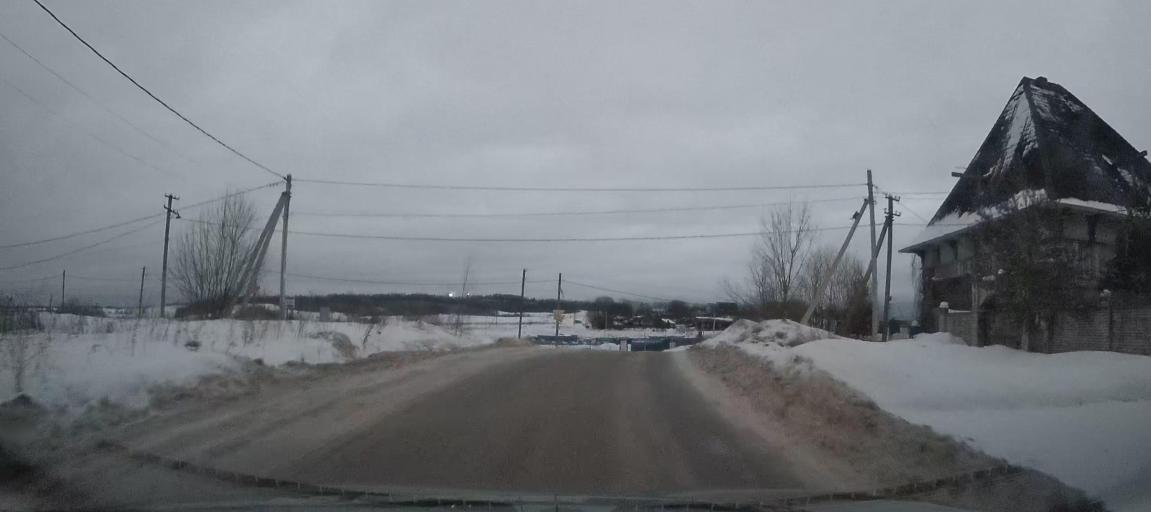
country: RU
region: Leningrad
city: Taytsy
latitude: 59.6968
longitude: 30.1413
